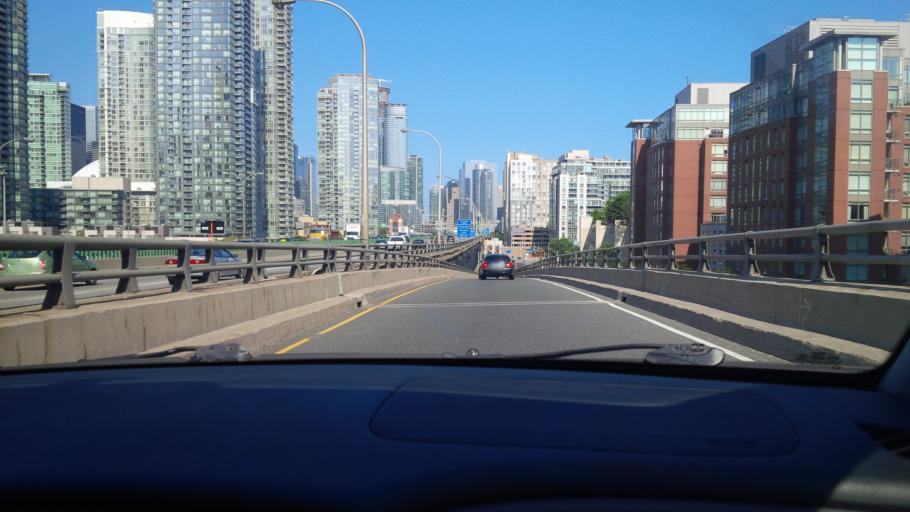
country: CA
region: Ontario
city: Toronto
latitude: 43.6378
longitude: -79.3968
